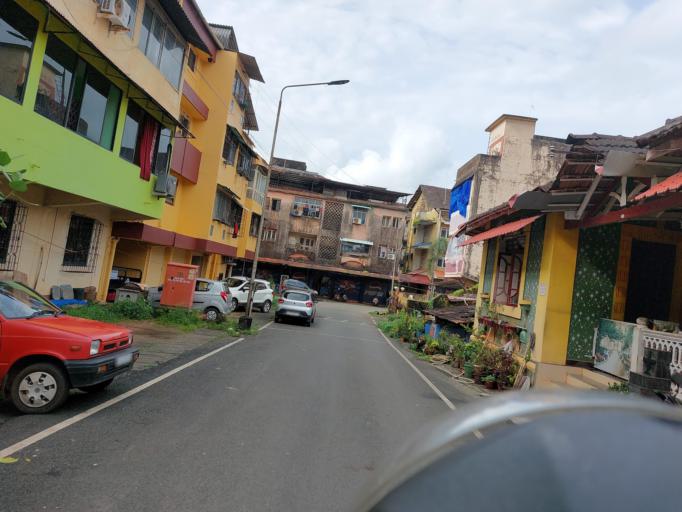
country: IN
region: Goa
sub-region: South Goa
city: Madgaon
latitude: 15.2764
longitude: 73.9546
